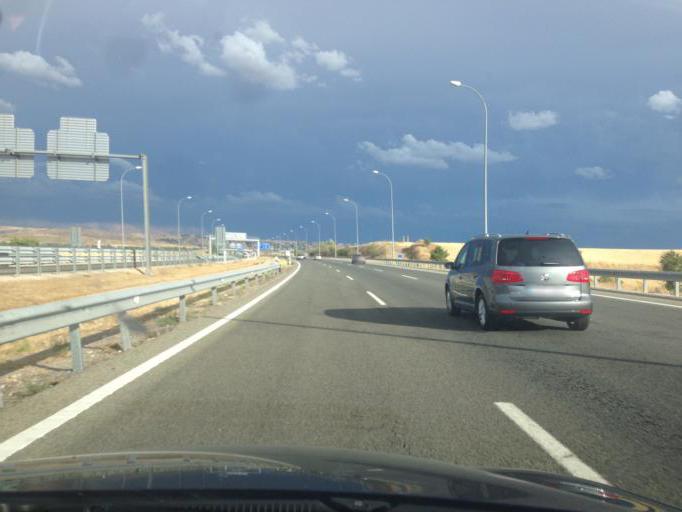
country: ES
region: Madrid
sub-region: Provincia de Madrid
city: San Sebastian de los Reyes
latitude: 40.5561
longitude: -3.5879
